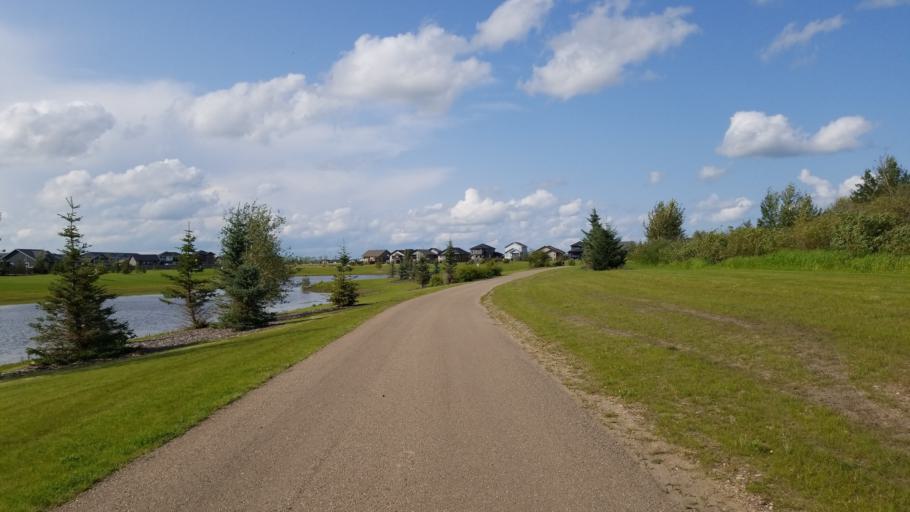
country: CA
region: Saskatchewan
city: Lloydminster
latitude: 53.2614
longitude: -110.0469
